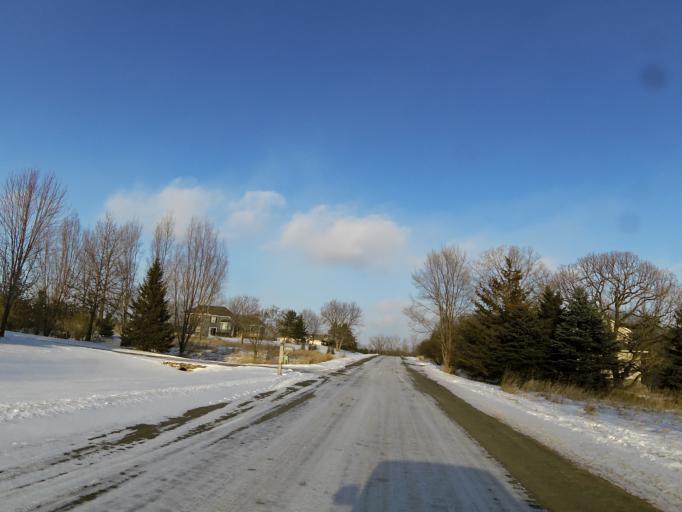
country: US
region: Minnesota
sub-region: Washington County
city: Lake Elmo
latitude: 44.9747
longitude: -92.8611
